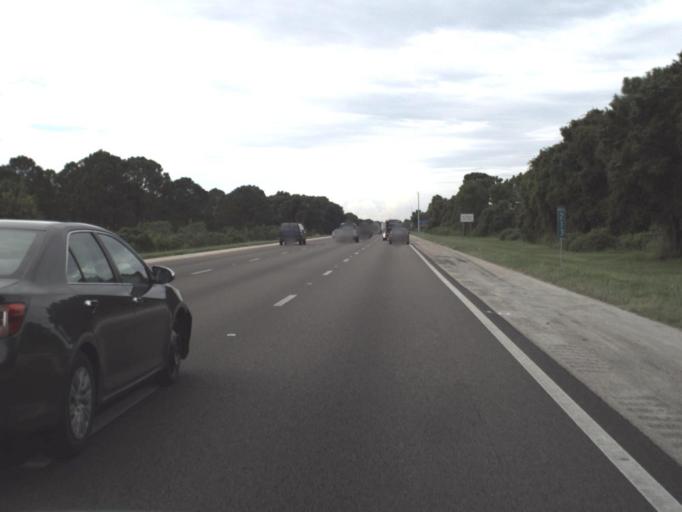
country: US
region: Florida
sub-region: Sarasota County
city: The Meadows
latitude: 27.3761
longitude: -82.4469
